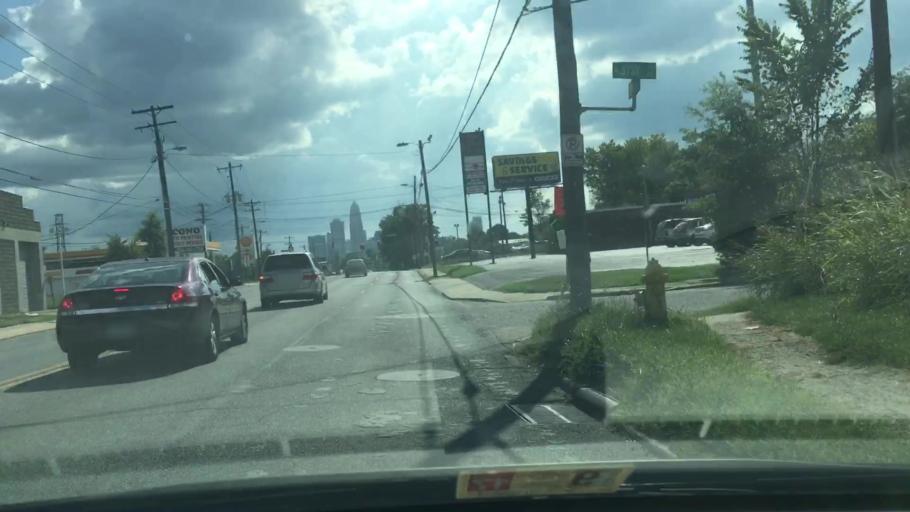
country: US
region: North Carolina
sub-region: Mecklenburg County
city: Charlotte
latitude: 35.2498
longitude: -80.8147
